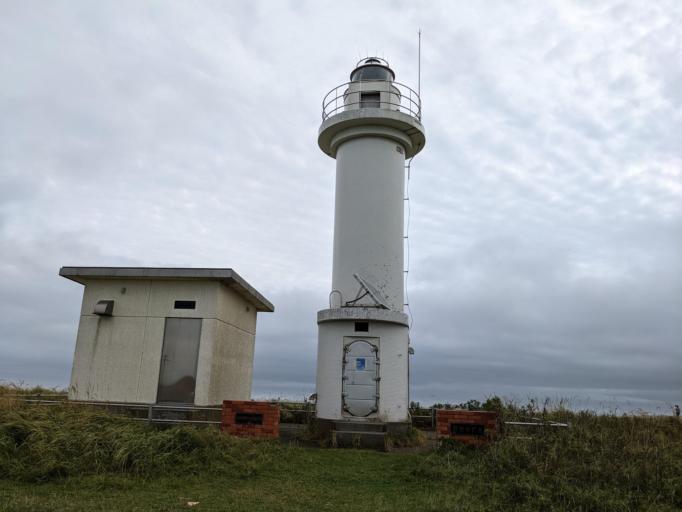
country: JP
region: Hokkaido
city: Shibetsu
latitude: 43.5637
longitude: 145.3474
